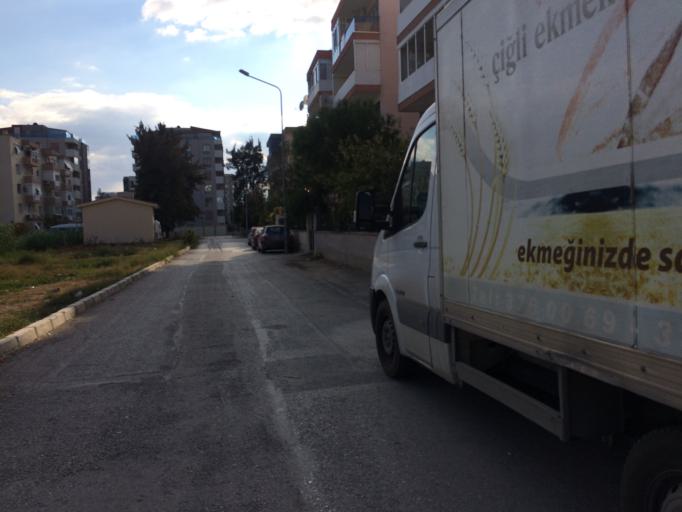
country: TR
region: Izmir
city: Karsiyaka
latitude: 38.4894
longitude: 27.0609
